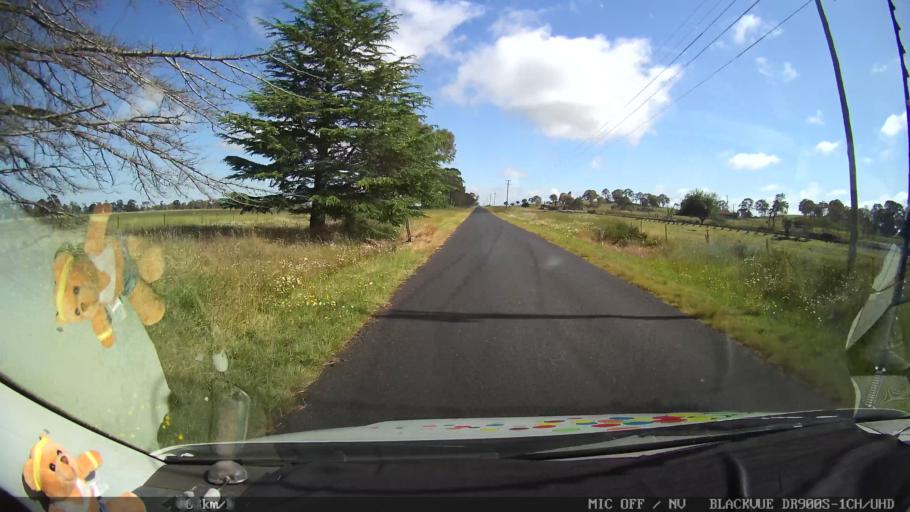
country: AU
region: New South Wales
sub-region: Guyra
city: Guyra
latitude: -30.2014
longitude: 151.6750
